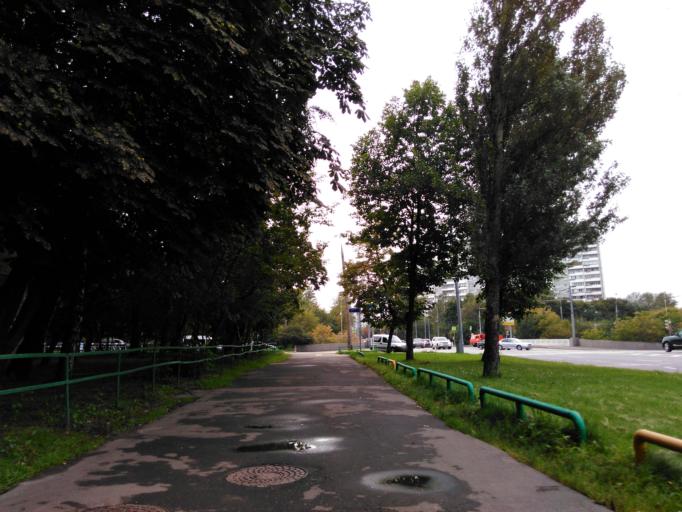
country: RU
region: Moskovskaya
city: Kastanayevo
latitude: 55.7110
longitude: 37.5076
